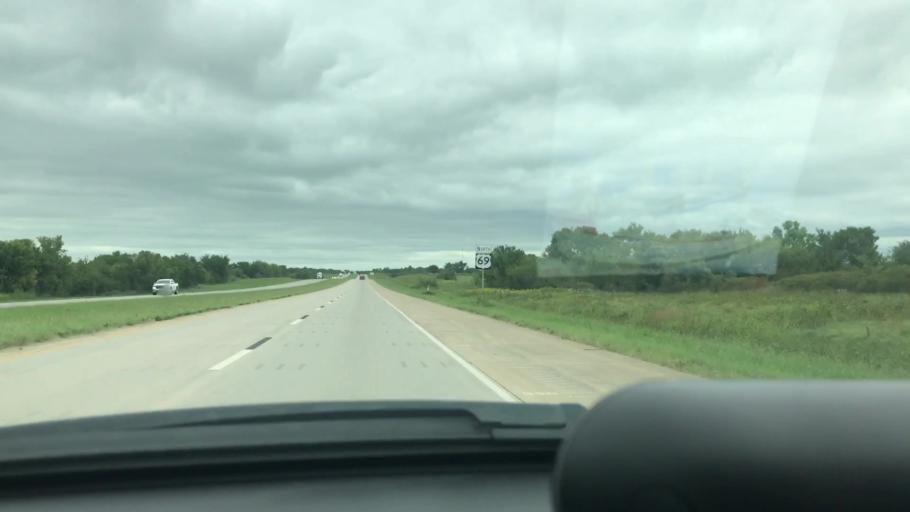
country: US
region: Oklahoma
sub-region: Mayes County
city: Chouteau
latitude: 36.0772
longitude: -95.3644
